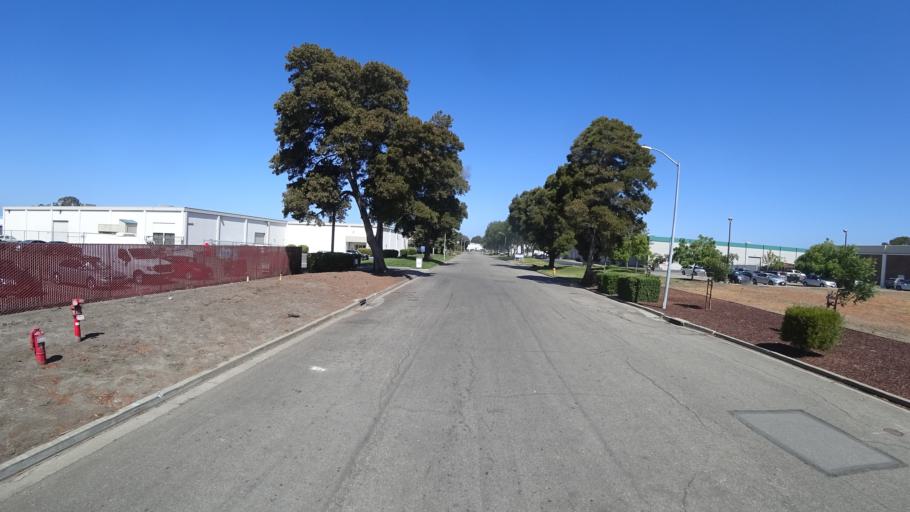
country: US
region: California
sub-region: Alameda County
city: San Lorenzo
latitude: 37.6584
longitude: -122.1286
